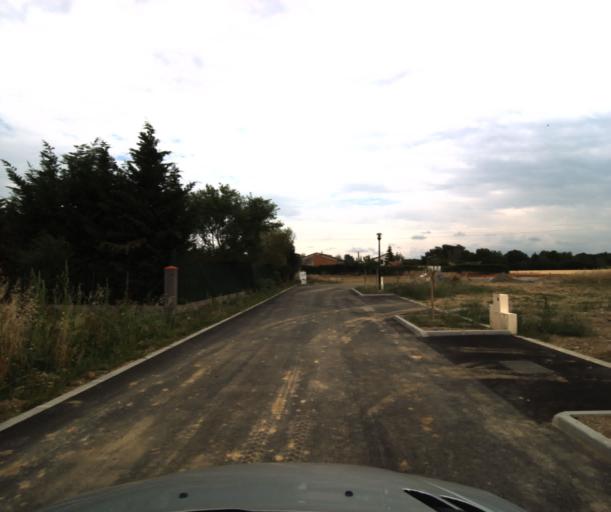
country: FR
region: Midi-Pyrenees
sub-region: Departement de la Haute-Garonne
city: Lherm
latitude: 43.4628
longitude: 1.2096
